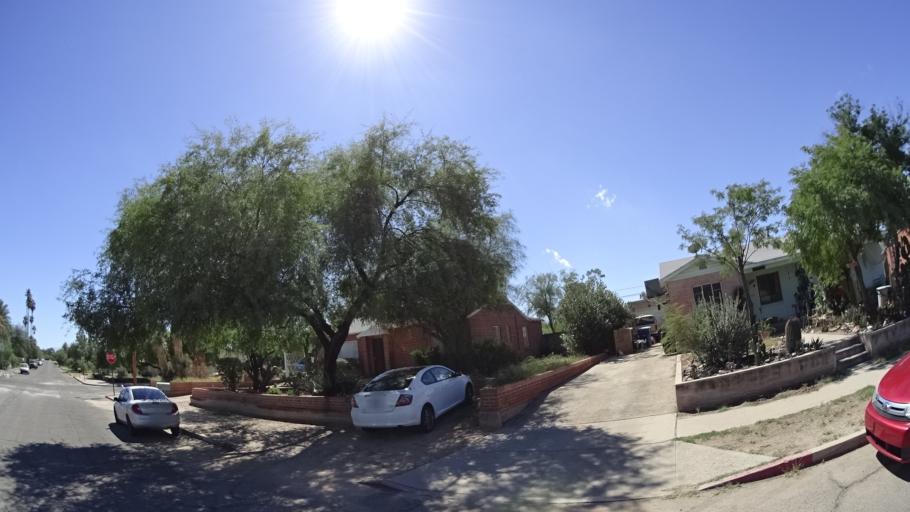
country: US
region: Arizona
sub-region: Pima County
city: Tucson
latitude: 32.2457
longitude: -110.9502
